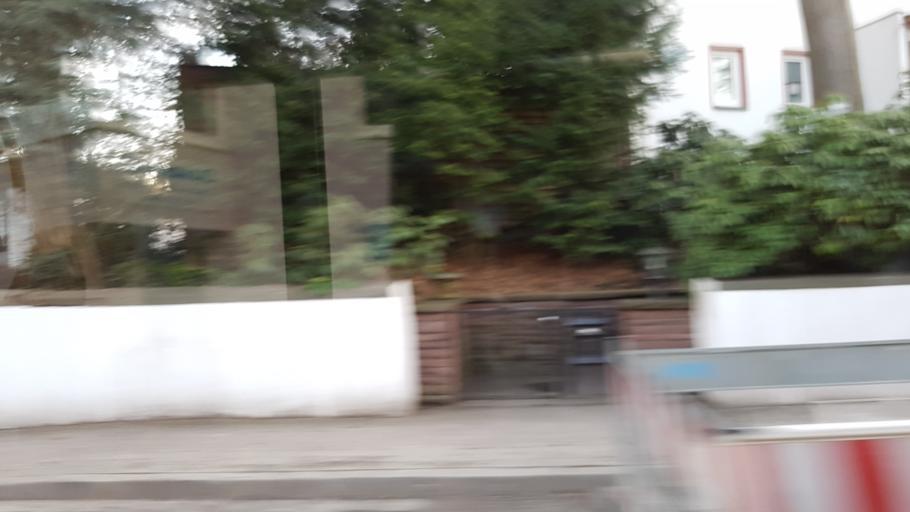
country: DE
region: Hesse
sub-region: Regierungsbezirk Darmstadt
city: Bad Homburg vor der Hoehe
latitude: 50.2306
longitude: 8.6027
